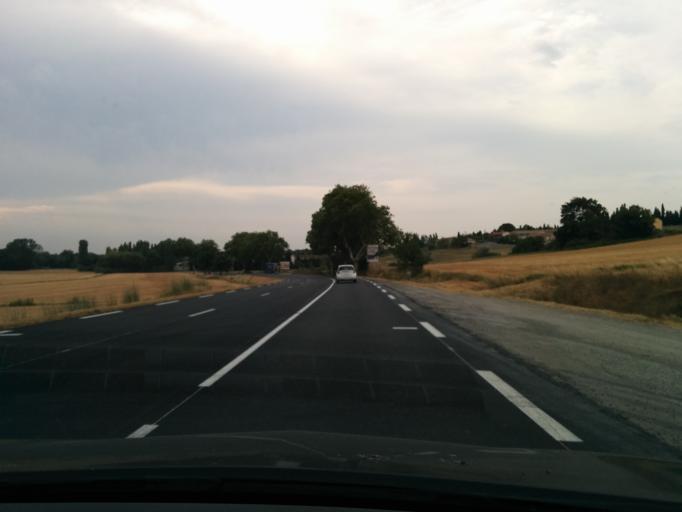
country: FR
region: Languedoc-Roussillon
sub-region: Departement de l'Aude
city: Villepinte
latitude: 43.2770
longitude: 2.0985
